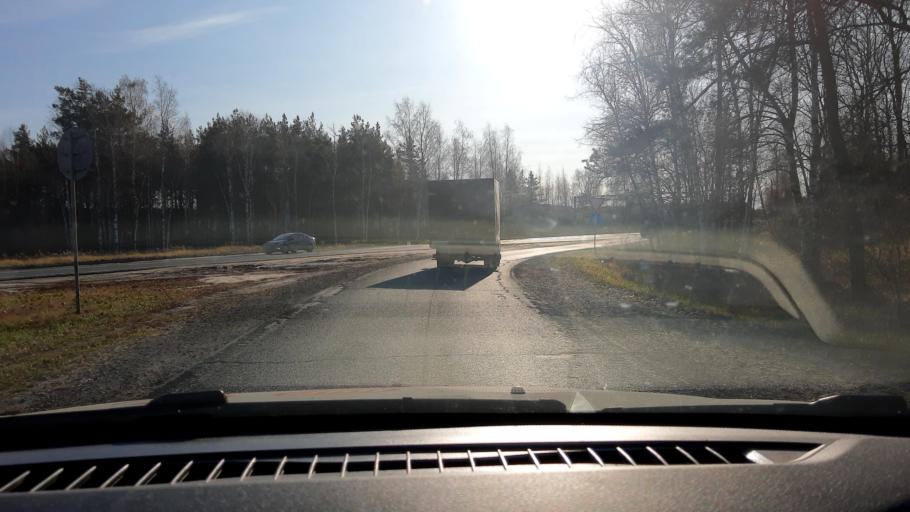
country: RU
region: Nizjnij Novgorod
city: Dzerzhinsk
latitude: 56.2967
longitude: 43.4760
